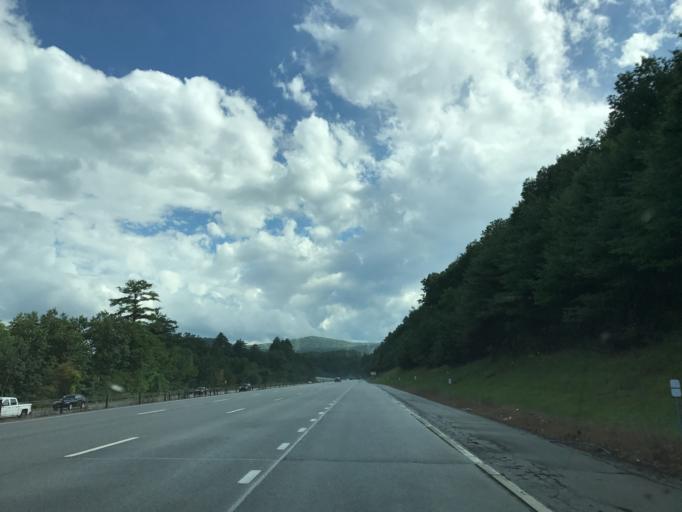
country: US
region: New York
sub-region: Warren County
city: Warrensburg
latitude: 43.4221
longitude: -73.7220
